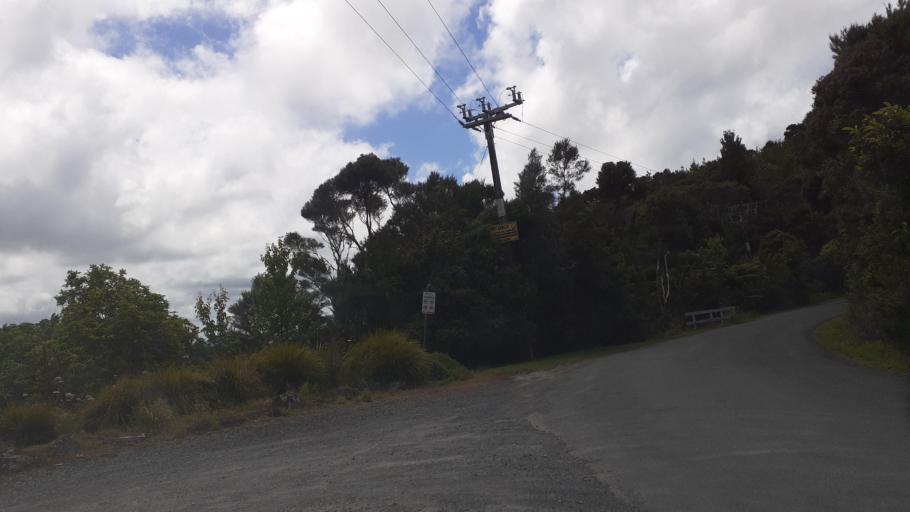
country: NZ
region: Northland
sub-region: Far North District
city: Paihia
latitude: -35.3125
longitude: 174.1128
